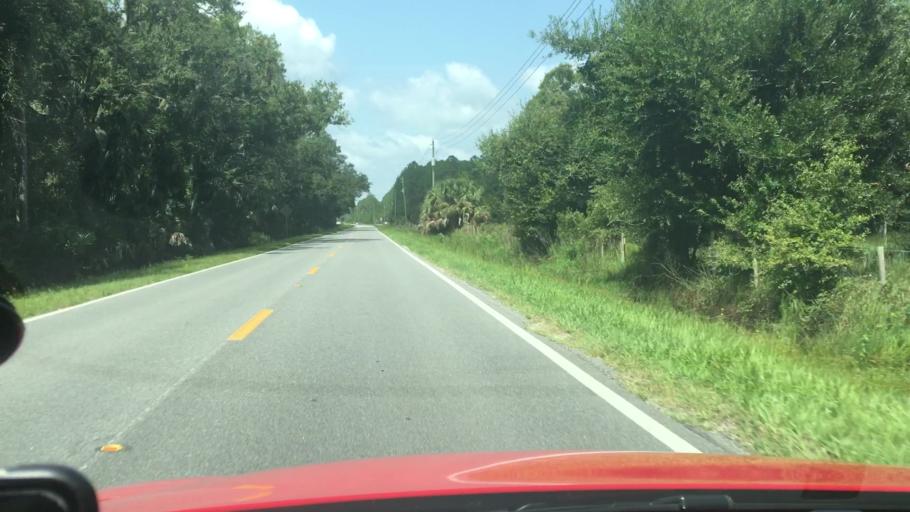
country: US
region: Florida
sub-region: Volusia County
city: Samsula-Spruce Creek
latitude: 29.0418
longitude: -81.0732
